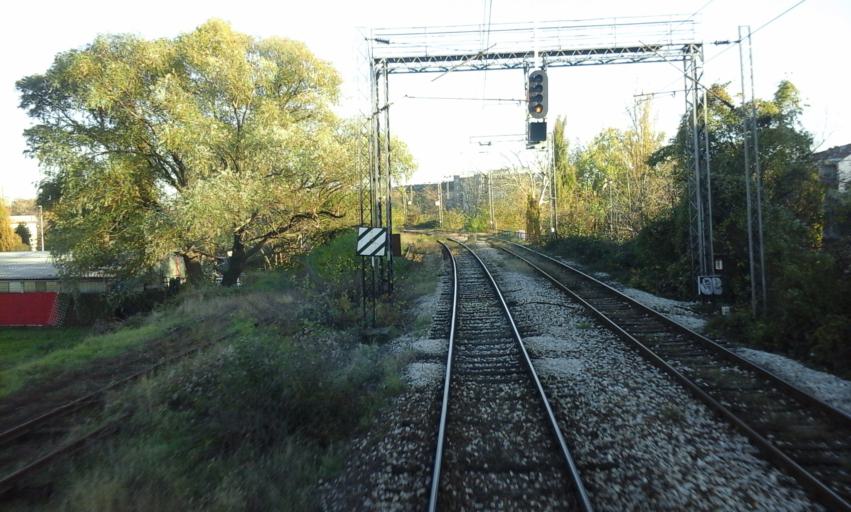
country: RS
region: Autonomna Pokrajina Vojvodina
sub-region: Juznobacki Okrug
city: Novi Sad
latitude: 45.2659
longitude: 19.8183
